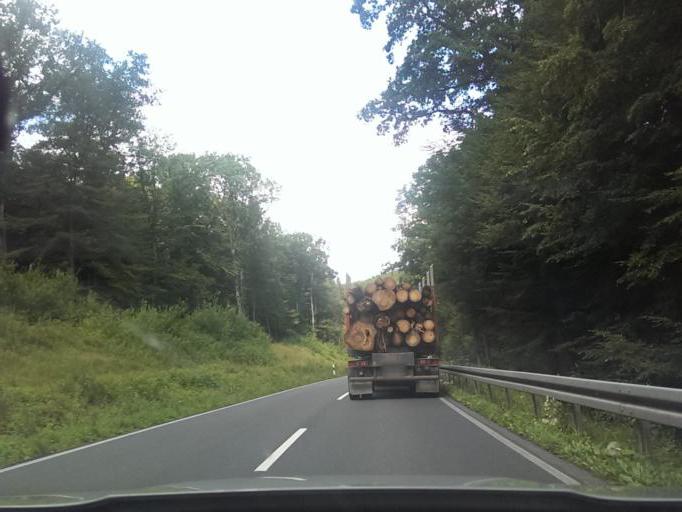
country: DE
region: North Rhine-Westphalia
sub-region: Regierungsbezirk Detmold
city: Hoexter
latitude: 51.8248
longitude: 9.3642
